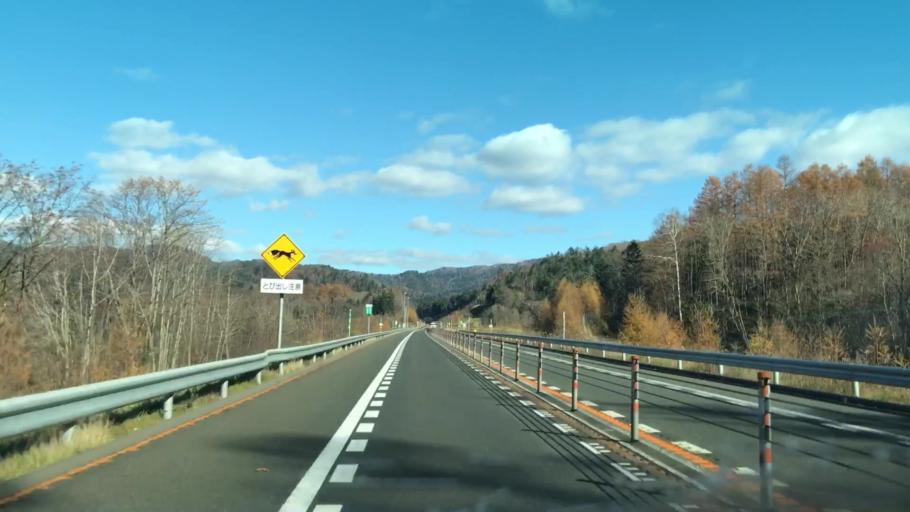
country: JP
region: Hokkaido
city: Shimo-furano
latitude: 42.9434
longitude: 142.2202
